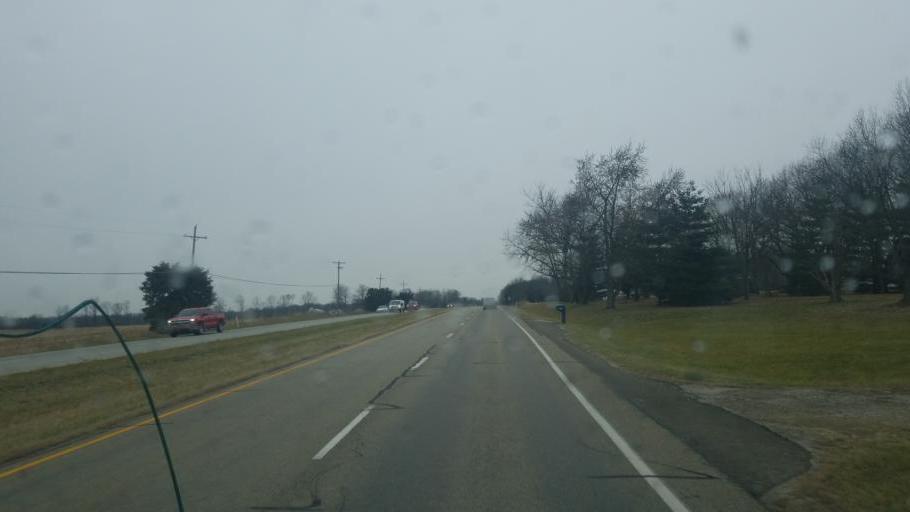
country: US
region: Indiana
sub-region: Henry County
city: Knightstown
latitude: 39.7919
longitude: -85.5966
